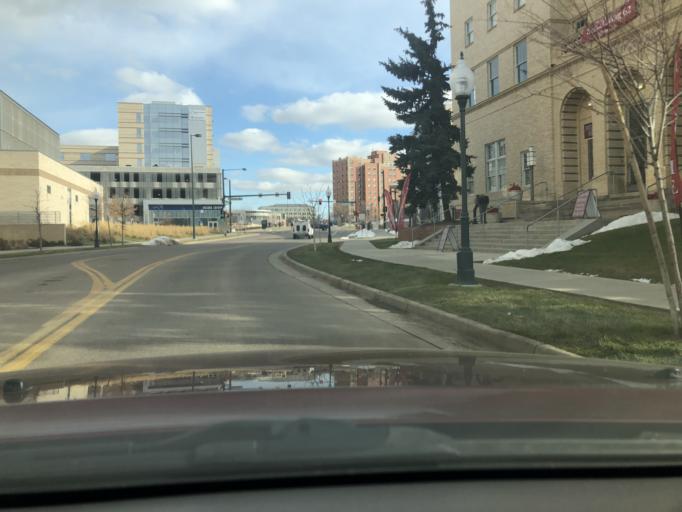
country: US
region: Colorado
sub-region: Denver County
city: Denver
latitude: 39.7461
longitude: -104.9746
